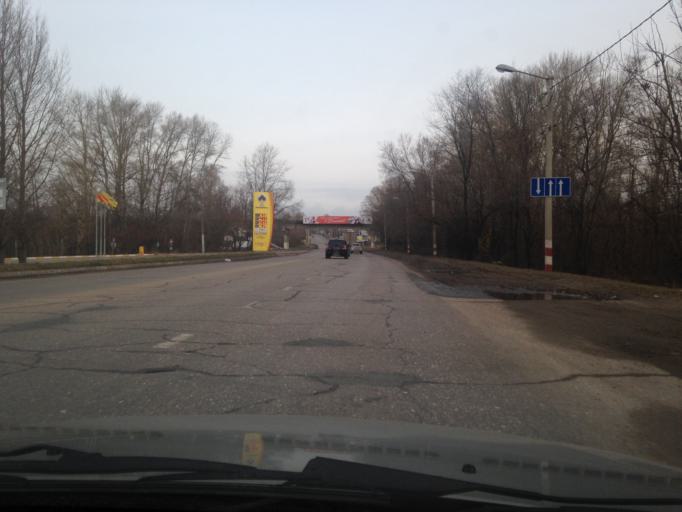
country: RU
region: Ulyanovsk
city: Novoul'yanovsk
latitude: 54.2132
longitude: 48.2974
